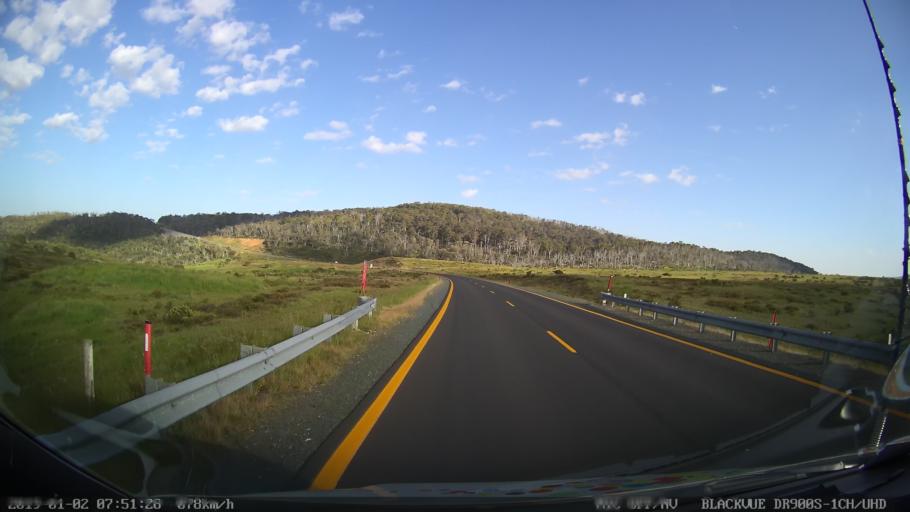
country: AU
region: New South Wales
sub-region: Tumut Shire
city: Tumut
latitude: -35.7180
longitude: 148.5305
